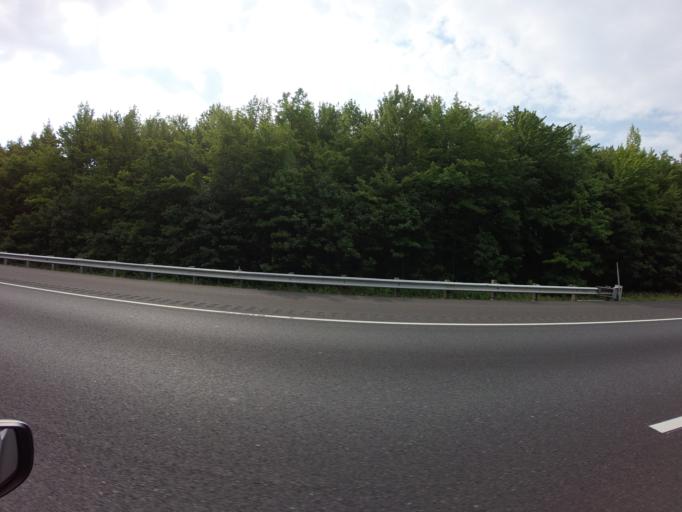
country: US
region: Maryland
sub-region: Baltimore County
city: White Marsh
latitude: 39.4034
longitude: -76.4228
